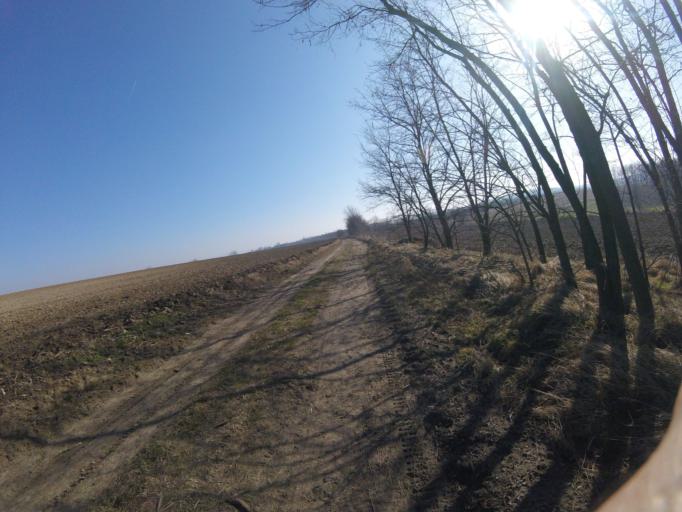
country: HU
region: Komarom-Esztergom
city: Bokod
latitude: 47.5248
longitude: 18.2071
